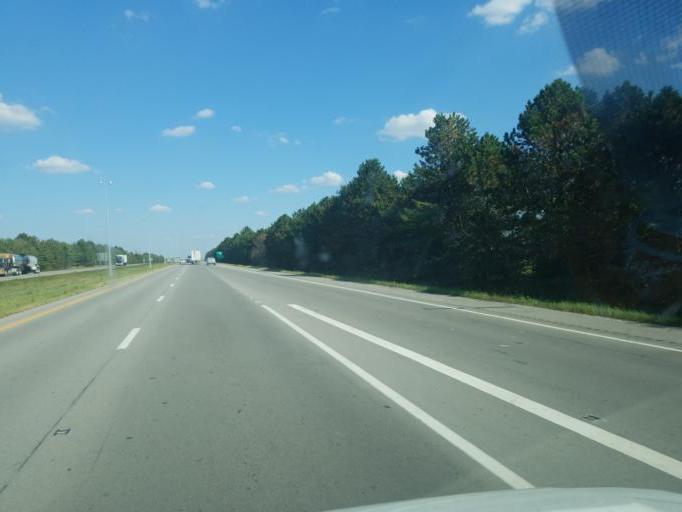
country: US
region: Ohio
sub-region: Wyandot County
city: Upper Sandusky
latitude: 40.8581
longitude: -83.2963
